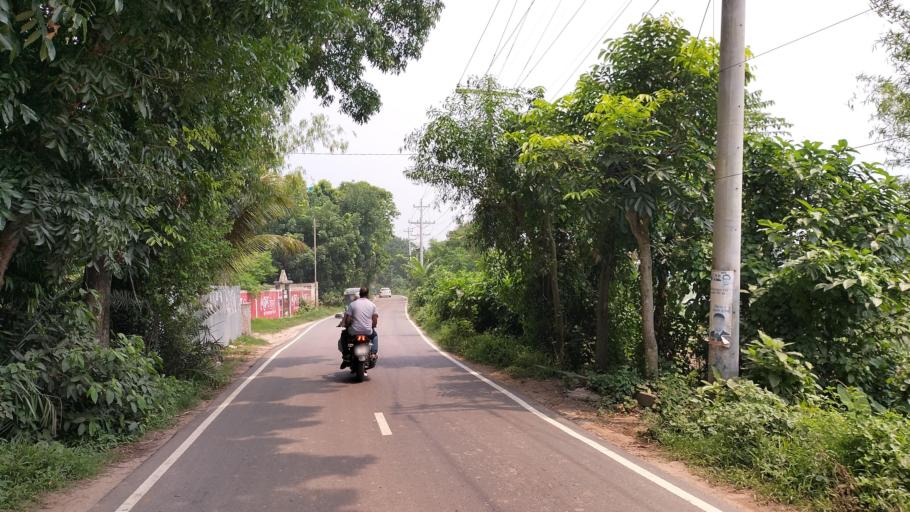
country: BD
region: Dhaka
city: Azimpur
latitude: 23.7219
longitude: 90.2746
